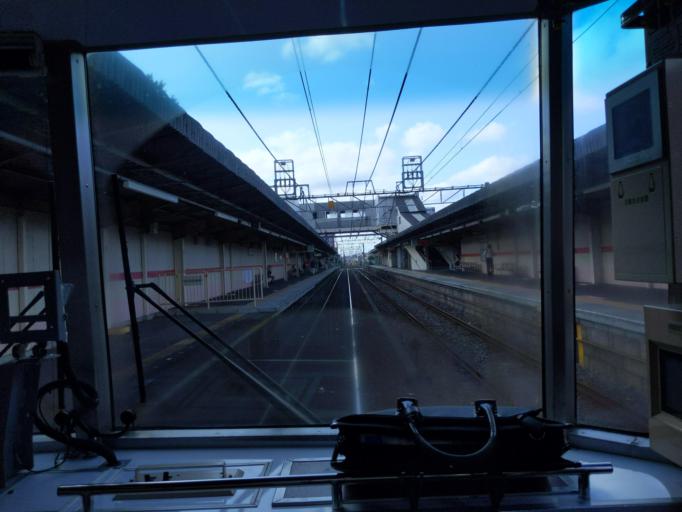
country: JP
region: Chiba
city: Shiroi
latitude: 35.7536
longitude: 140.0245
